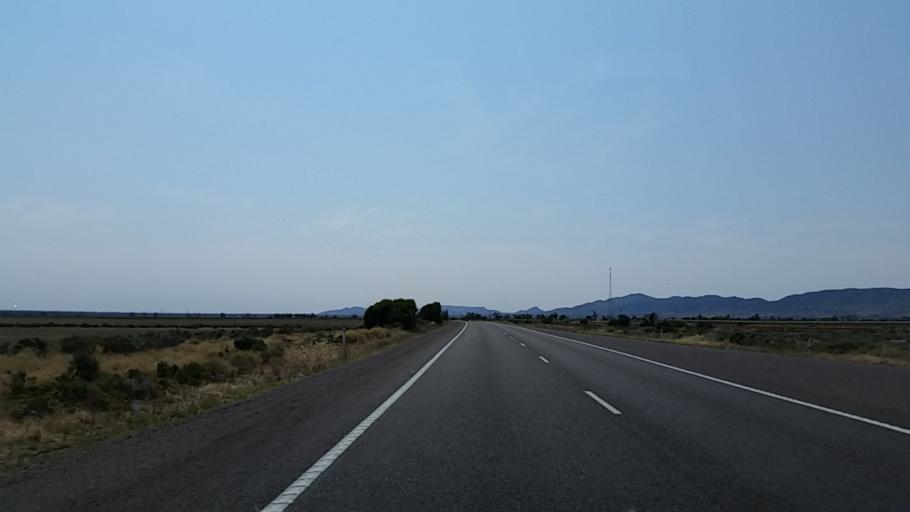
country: AU
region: South Australia
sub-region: Port Augusta
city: Port Augusta
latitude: -32.7039
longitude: 137.9422
